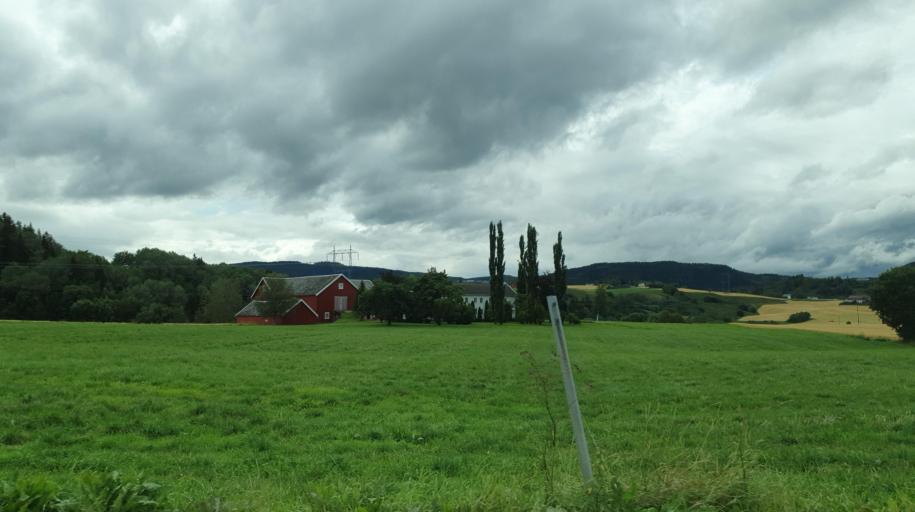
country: NO
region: Nord-Trondelag
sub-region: Stjordal
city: Stjordalshalsen
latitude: 63.4339
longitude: 10.9496
